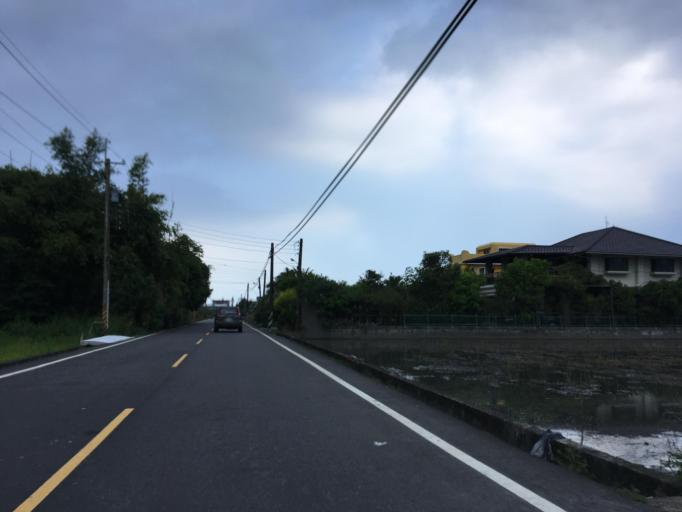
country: TW
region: Taiwan
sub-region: Yilan
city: Yilan
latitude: 24.6992
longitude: 121.7412
